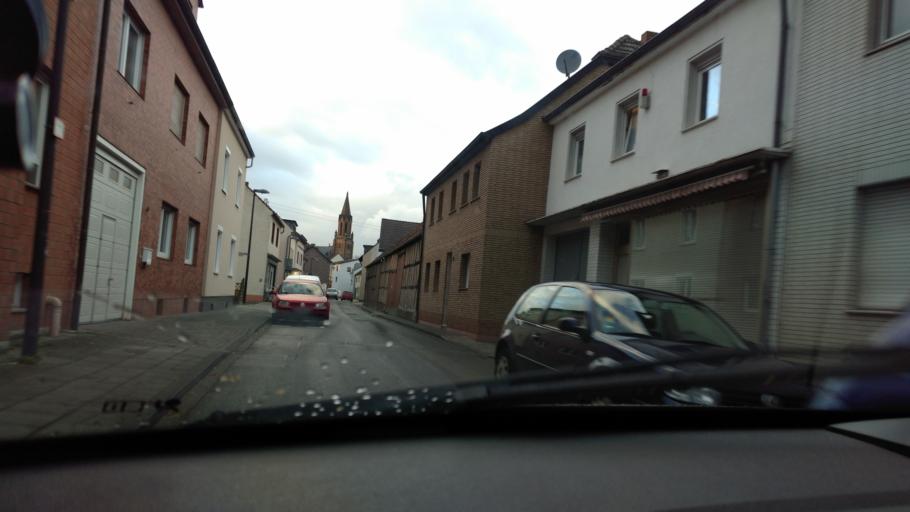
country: DE
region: North Rhine-Westphalia
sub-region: Regierungsbezirk Koln
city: Bonn
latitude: 50.7729
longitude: 7.0945
